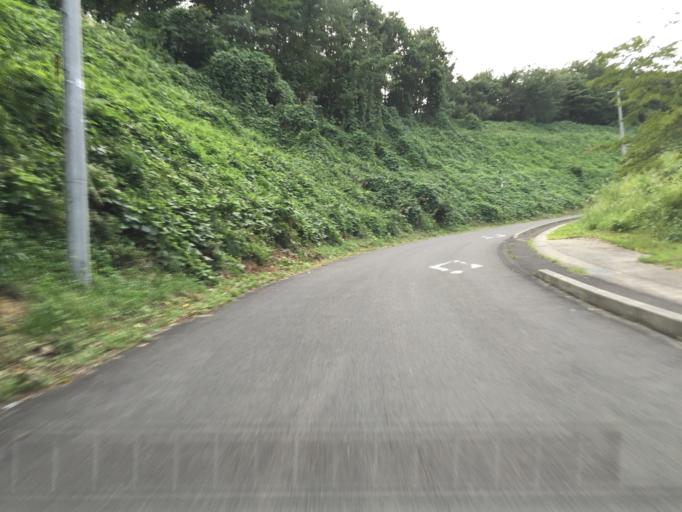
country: JP
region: Fukushima
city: Fukushima-shi
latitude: 37.6696
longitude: 140.5790
